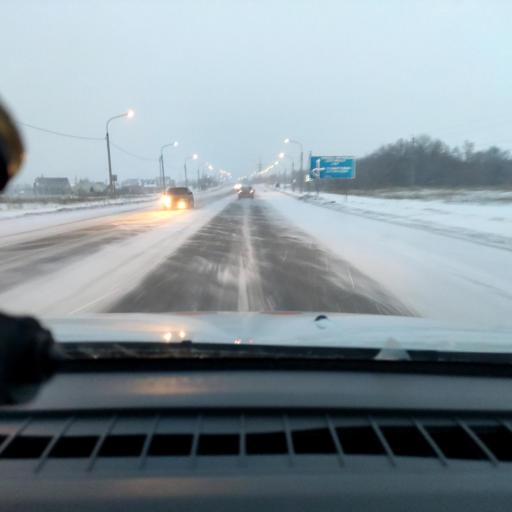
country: RU
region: Samara
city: Kinel'-Cherkassy
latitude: 53.4219
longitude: 51.4785
